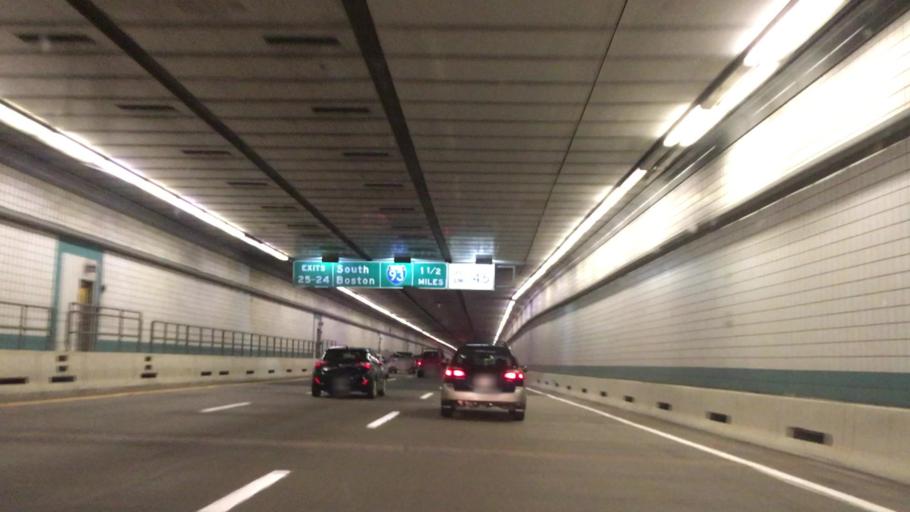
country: US
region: Massachusetts
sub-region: Suffolk County
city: Chelsea
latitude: 42.3630
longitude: -71.0245
